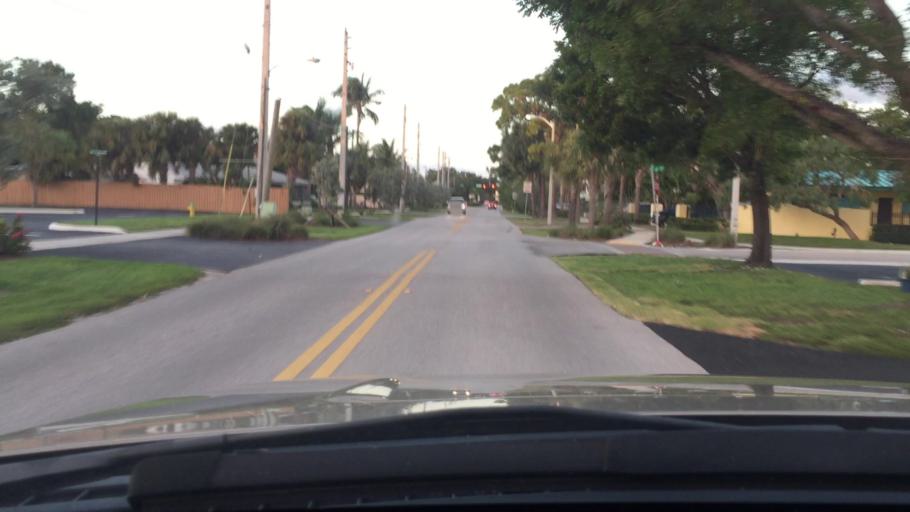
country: US
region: Florida
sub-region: Broward County
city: Deerfield Beach
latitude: 26.3132
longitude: -80.0876
